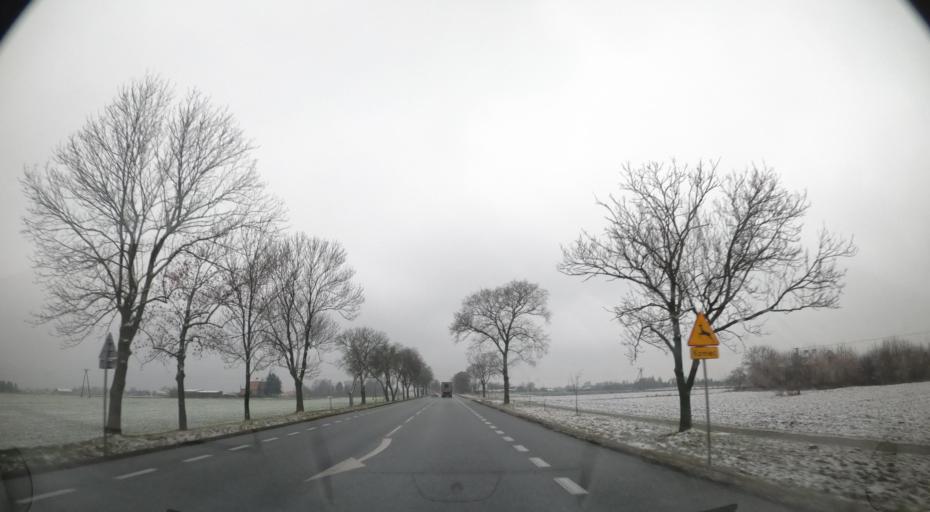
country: PL
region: Masovian Voivodeship
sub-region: Powiat sochaczewski
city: Sochaczew
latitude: 52.2256
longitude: 20.2799
